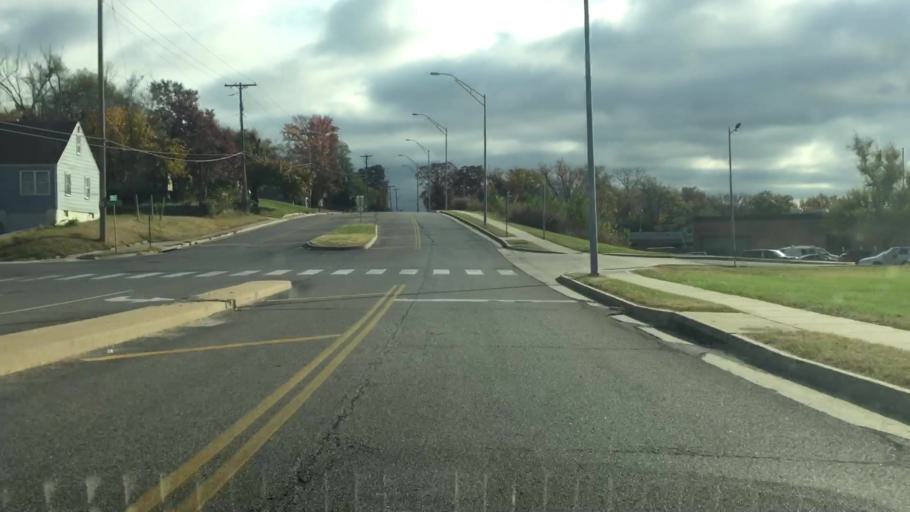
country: US
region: Kansas
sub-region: Johnson County
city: Leawood
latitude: 38.9904
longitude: -94.5507
